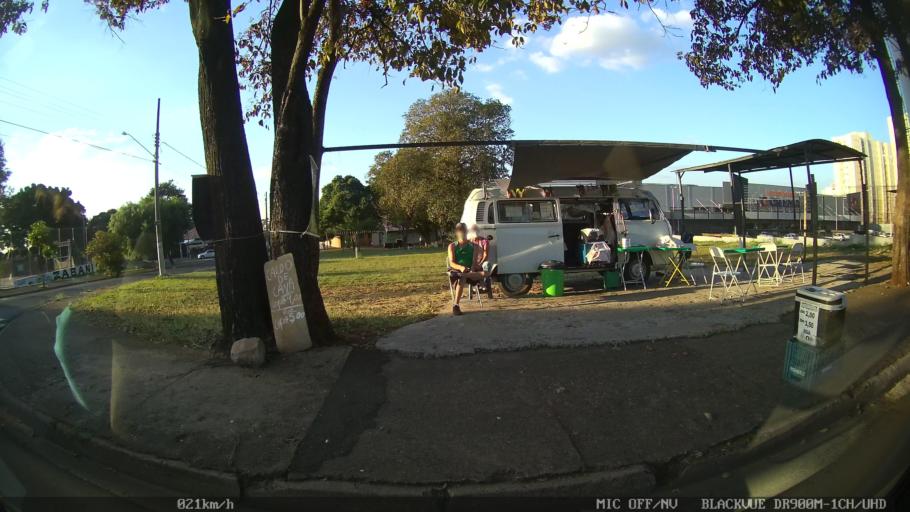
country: BR
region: Sao Paulo
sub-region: Santa Barbara D'Oeste
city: Santa Barbara d'Oeste
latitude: -22.7350
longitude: -47.3748
